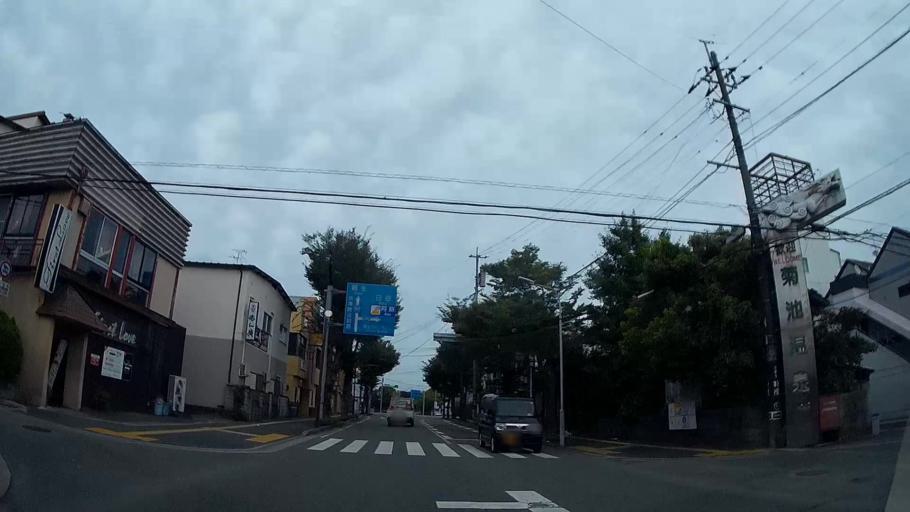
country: JP
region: Kumamoto
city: Kikuchi
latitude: 32.9837
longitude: 130.8148
